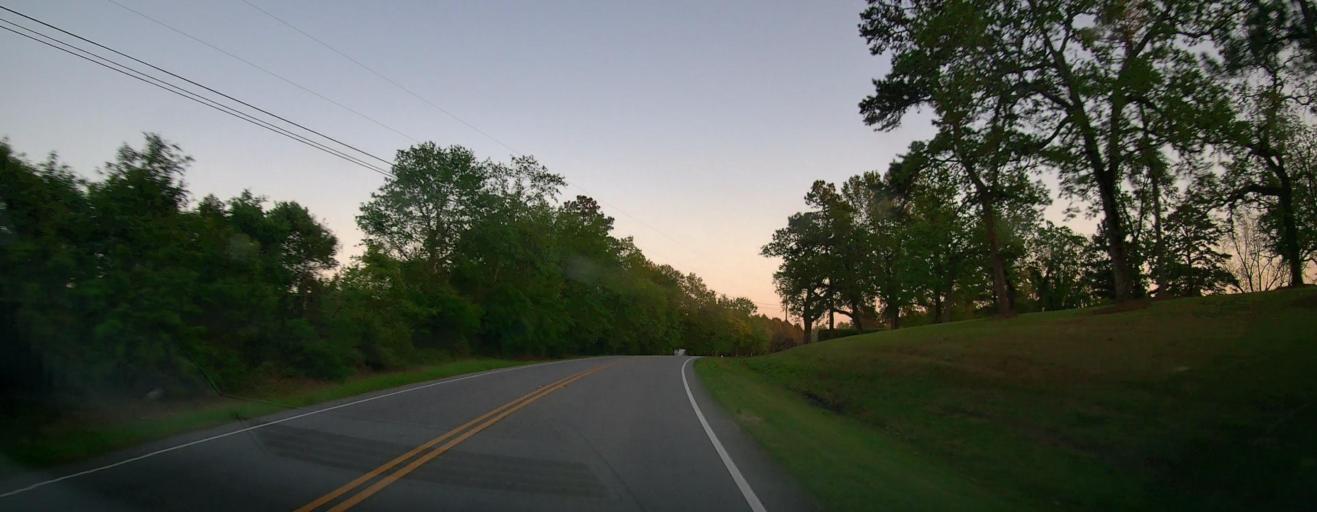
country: US
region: Georgia
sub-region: Marion County
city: Buena Vista
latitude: 32.3481
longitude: -84.5327
